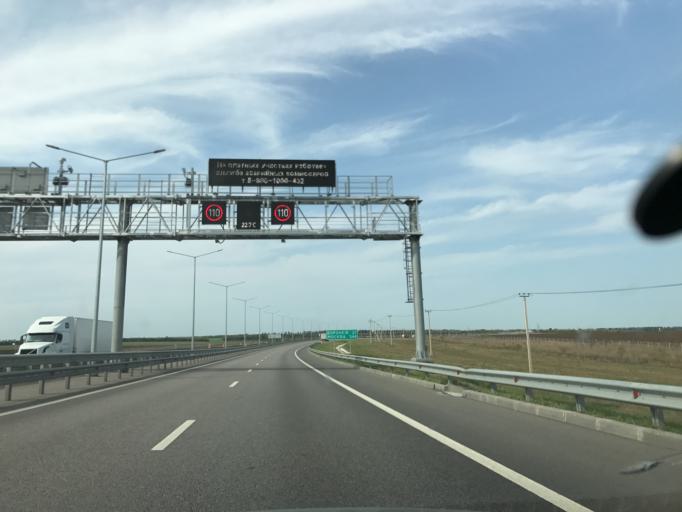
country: RU
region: Voronezj
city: Kashirskoye
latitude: 51.4839
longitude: 39.5400
